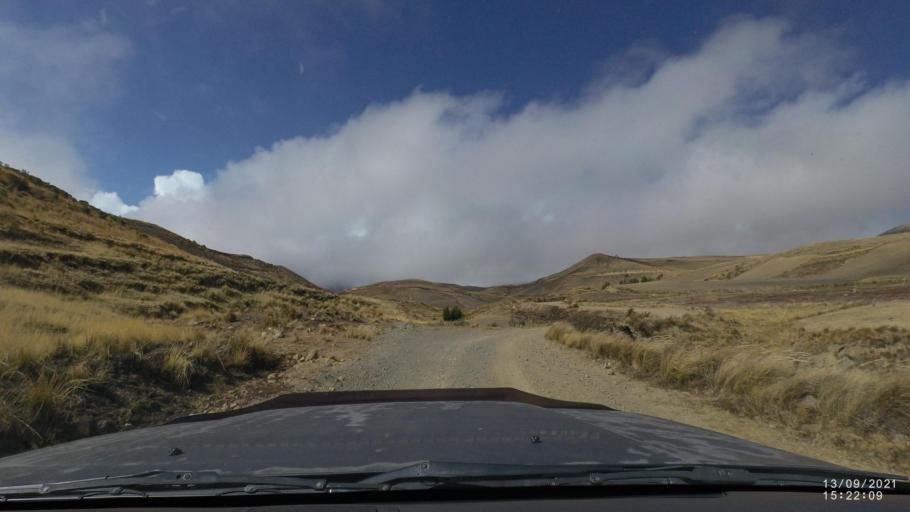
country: BO
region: Cochabamba
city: Colomi
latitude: -17.3574
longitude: -65.7807
